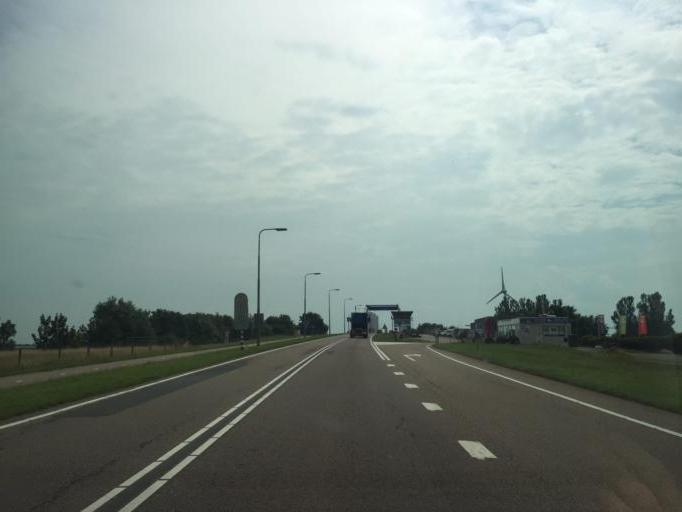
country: NL
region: North Holland
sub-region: Gemeente Enkhuizen
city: Enkhuizen
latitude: 52.6941
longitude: 5.2800
